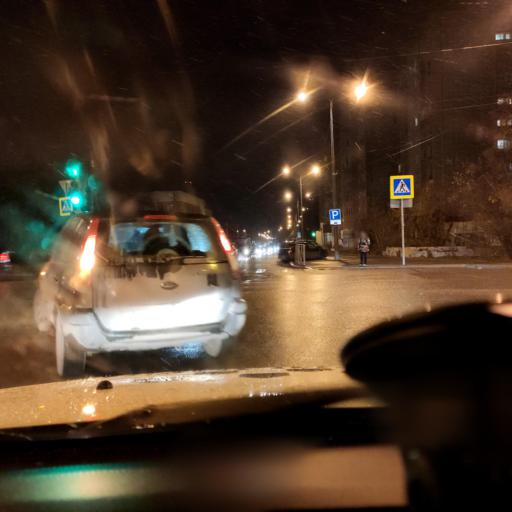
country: RU
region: Perm
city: Perm
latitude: 57.9773
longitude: 56.2044
